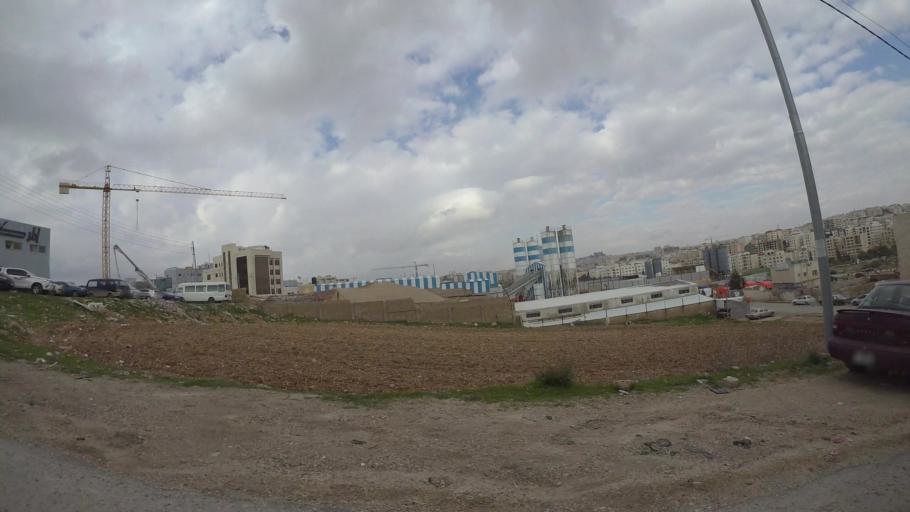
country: JO
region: Amman
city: Wadi as Sir
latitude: 31.9380
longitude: 35.8466
